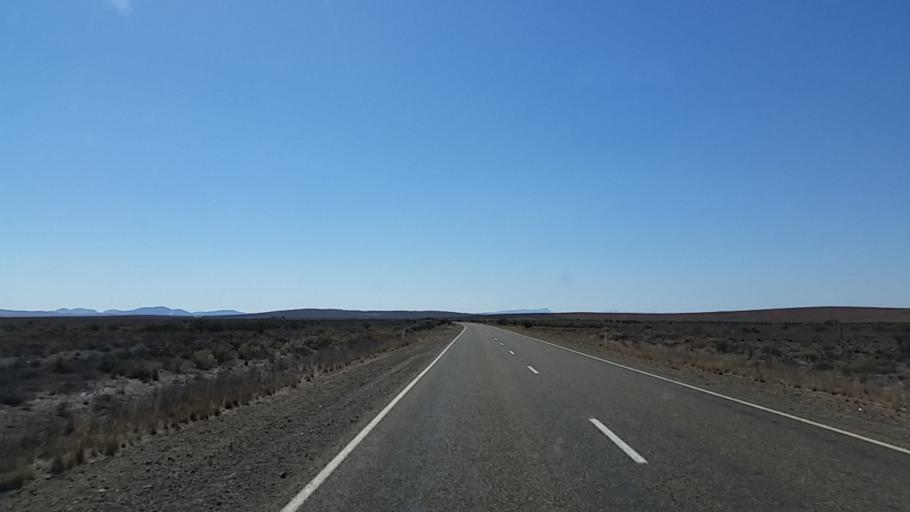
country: AU
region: South Australia
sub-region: Flinders Ranges
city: Quorn
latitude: -32.1179
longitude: 138.5057
